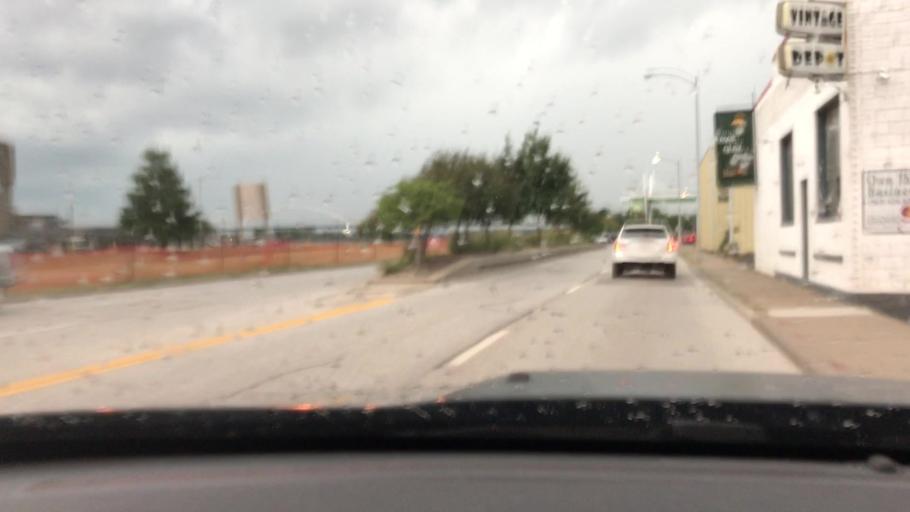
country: US
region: Iowa
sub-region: Scott County
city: Davenport
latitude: 41.5206
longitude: -90.5701
